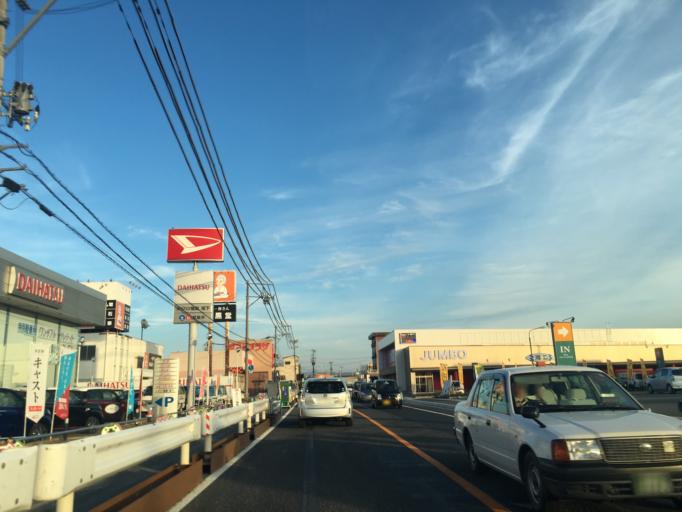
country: JP
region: Fukushima
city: Kitakata
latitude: 37.5638
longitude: 139.8234
